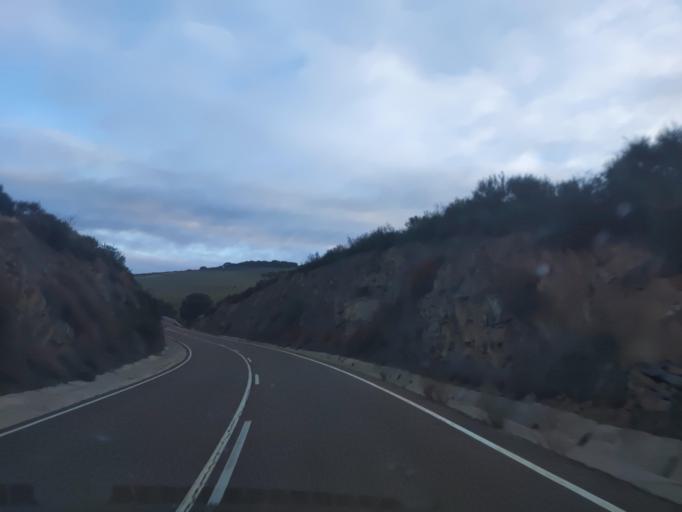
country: ES
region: Castille and Leon
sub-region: Provincia de Salamanca
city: Castillejo de Martin Viejo
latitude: 40.7281
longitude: -6.6368
